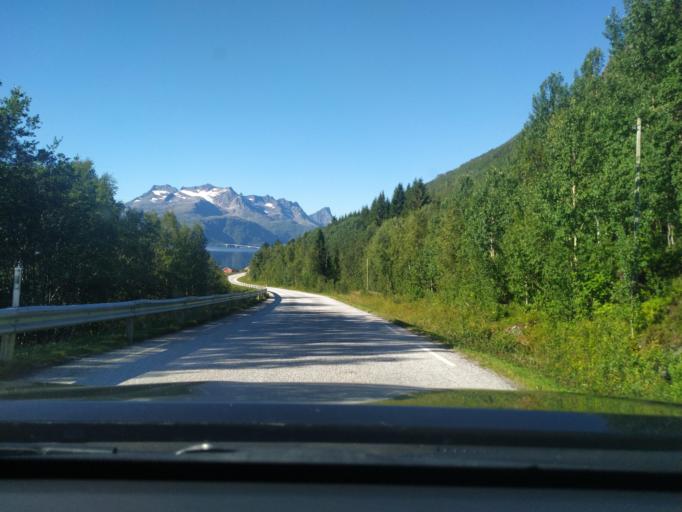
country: NO
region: Troms
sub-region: Dyroy
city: Brostadbotn
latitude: 68.9226
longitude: 17.6303
